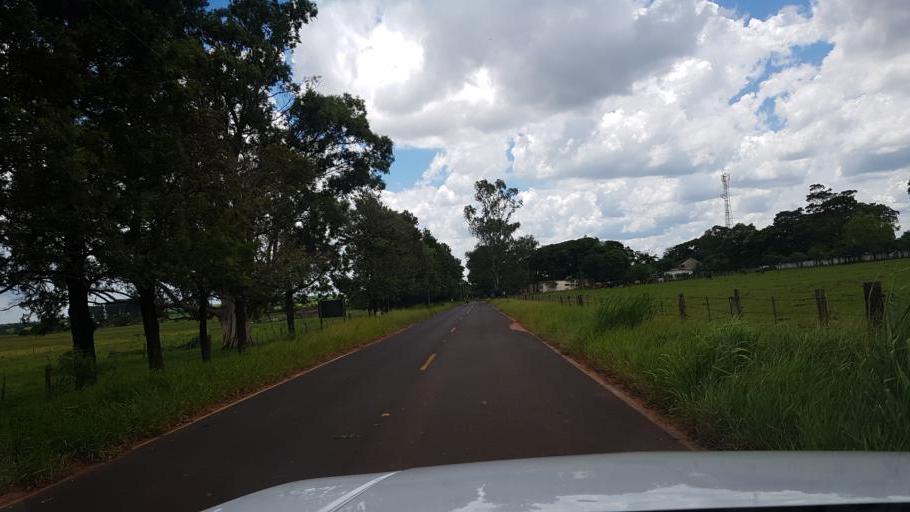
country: BR
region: Sao Paulo
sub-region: Paraguacu Paulista
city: Paraguacu Paulista
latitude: -22.3555
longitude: -50.6253
